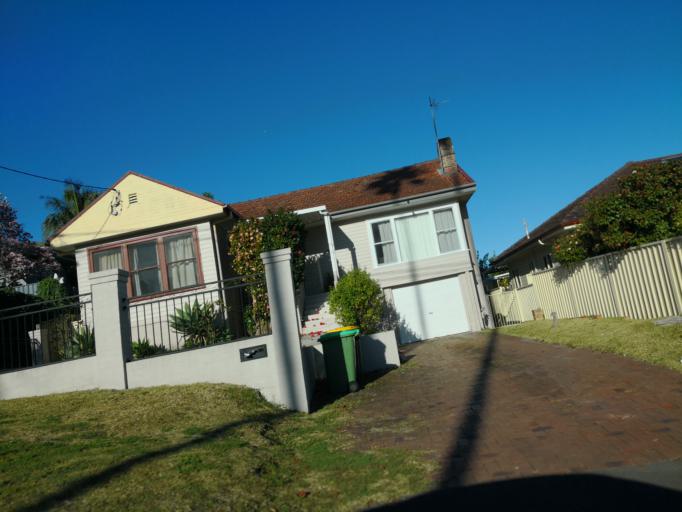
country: AU
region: New South Wales
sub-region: Gosford Shire
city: Narara
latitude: -33.4018
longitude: 151.3504
